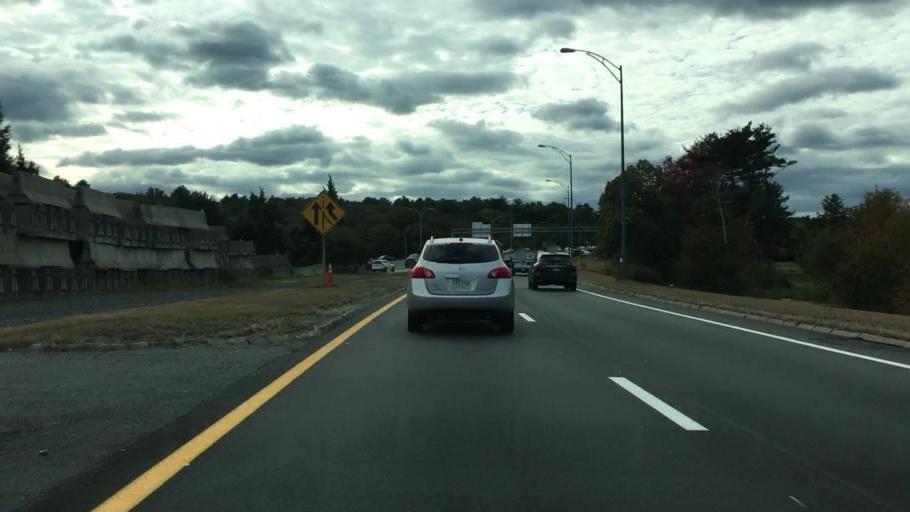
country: US
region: Massachusetts
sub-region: Middlesex County
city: Weston
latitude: 42.3397
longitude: -71.2733
